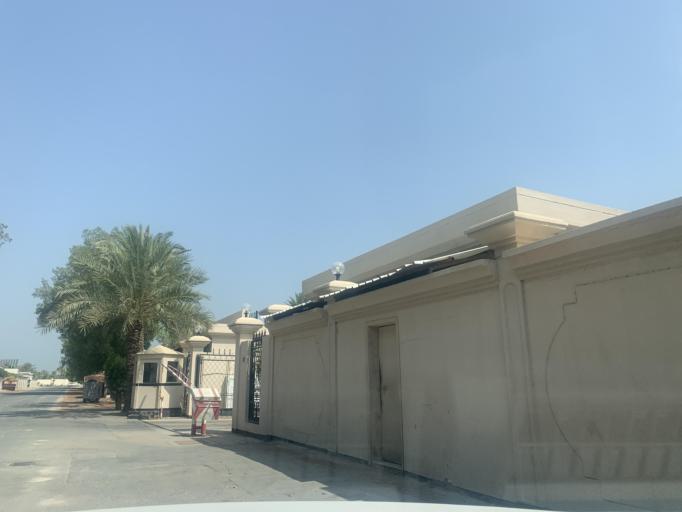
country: BH
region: Central Governorate
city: Madinat Hamad
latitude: 26.1696
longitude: 50.4614
